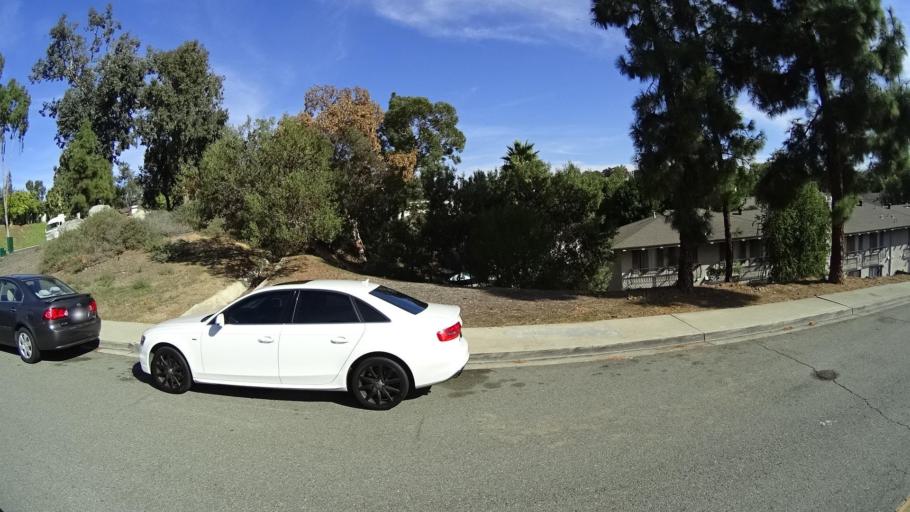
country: US
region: California
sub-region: San Diego County
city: Spring Valley
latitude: 32.7282
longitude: -116.9735
